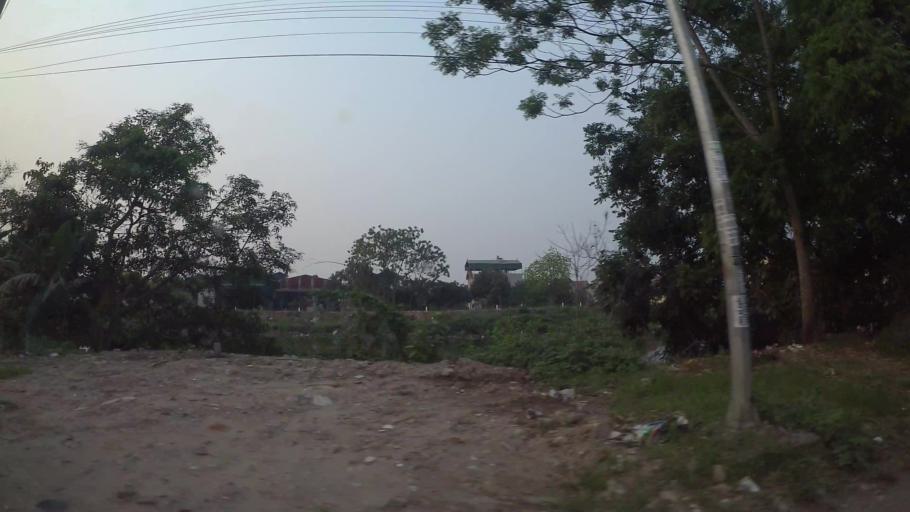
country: VN
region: Ha Noi
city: Thuong Tin
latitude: 20.8696
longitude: 105.8224
